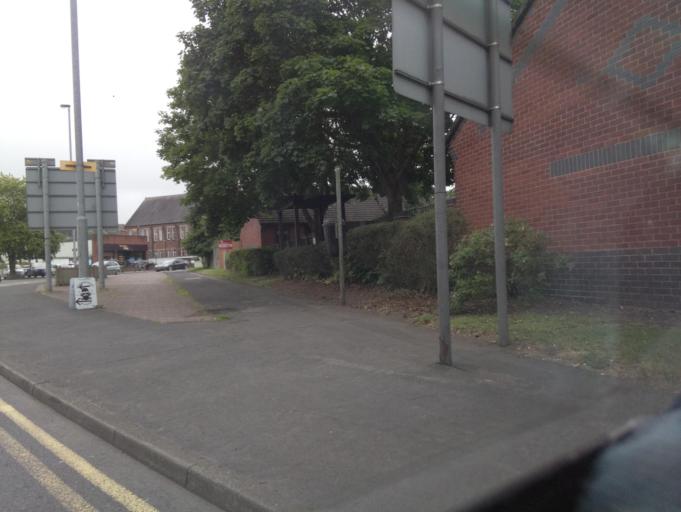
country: GB
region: England
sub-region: Staffordshire
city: Burton upon Trent
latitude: 52.7950
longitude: -1.6210
